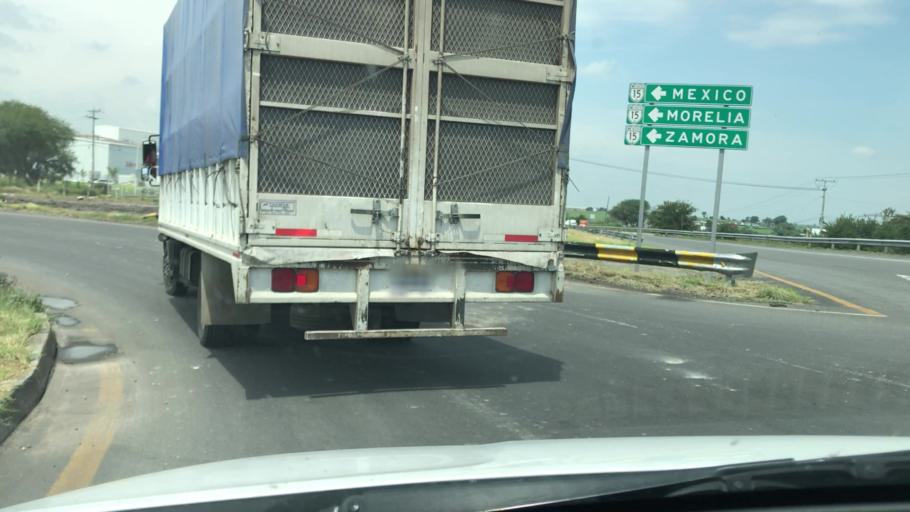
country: MX
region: Michoacan
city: Vistahermosa de Negrete
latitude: 20.2689
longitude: -102.4463
